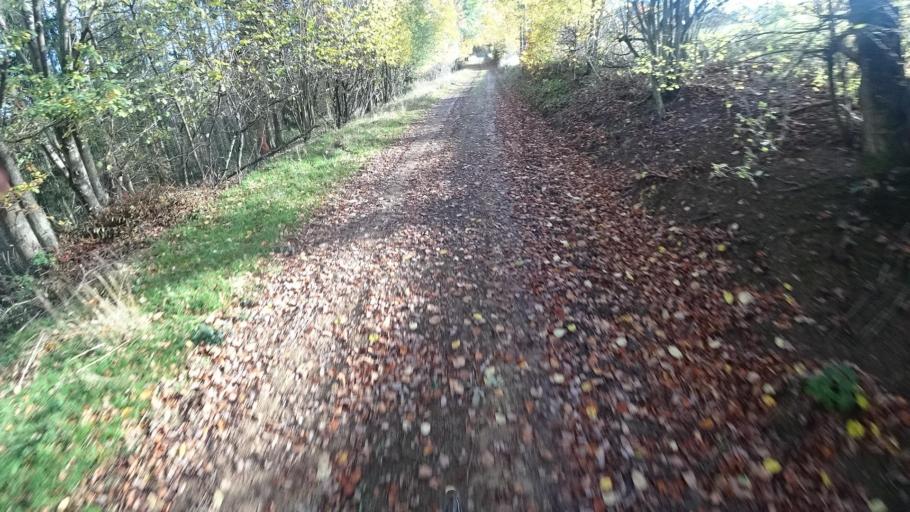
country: DE
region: Rheinland-Pfalz
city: Lind
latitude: 50.4865
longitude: 6.9430
